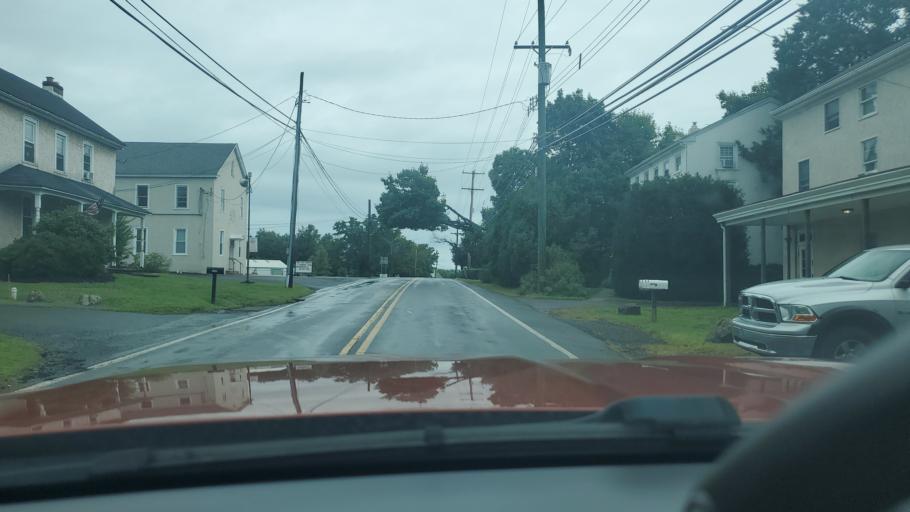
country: US
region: Pennsylvania
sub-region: Montgomery County
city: Spring Mount
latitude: 40.2788
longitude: -75.4807
